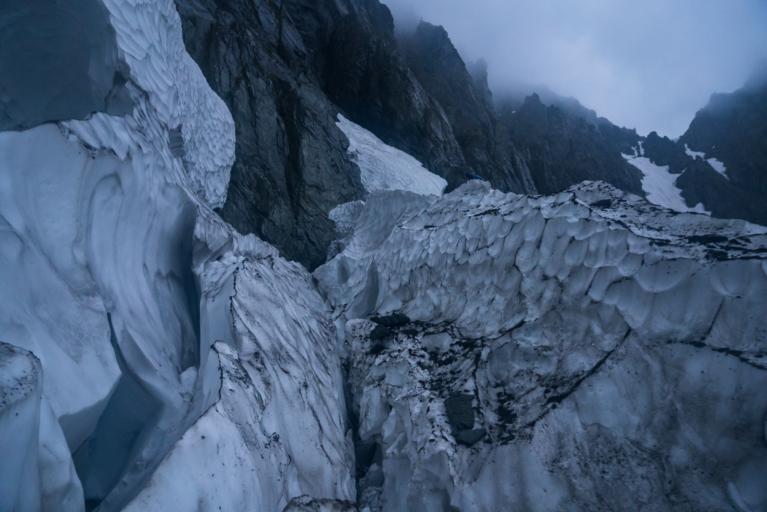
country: RU
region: Komi Republic
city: Synya
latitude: 64.7811
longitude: 58.8850
